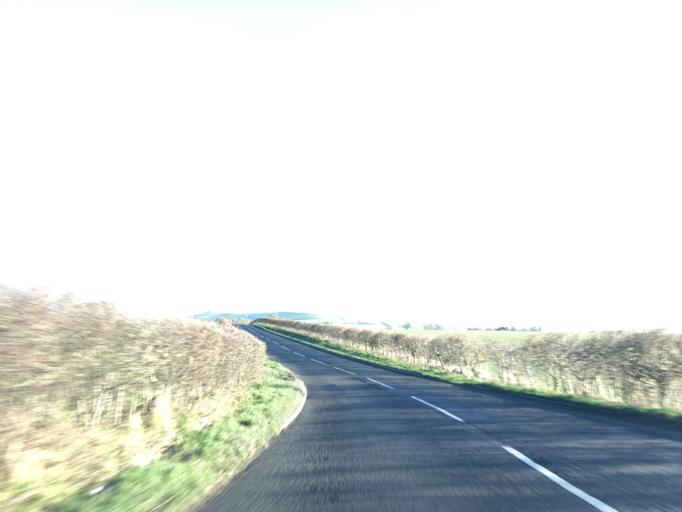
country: GB
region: England
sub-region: Borough of Swindon
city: Chiseldon
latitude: 51.5184
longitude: -1.7445
